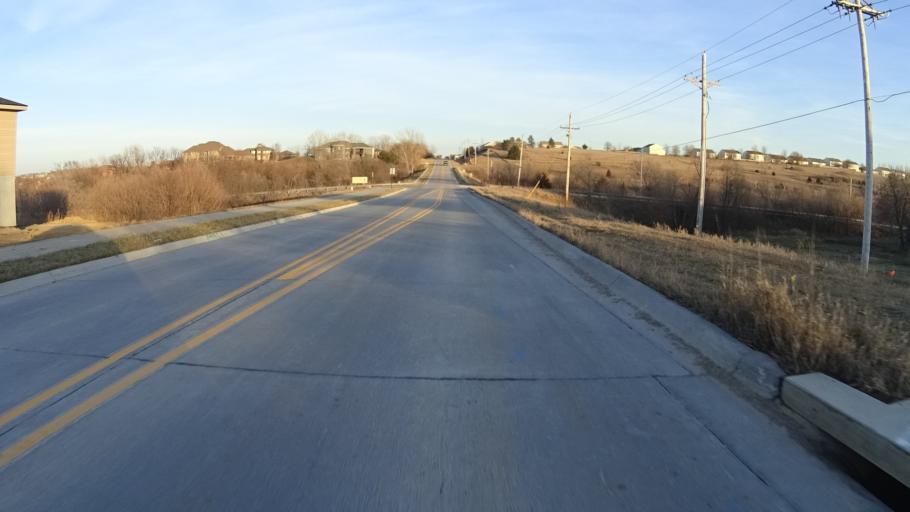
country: US
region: Nebraska
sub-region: Sarpy County
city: Papillion
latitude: 41.1327
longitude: -96.0765
